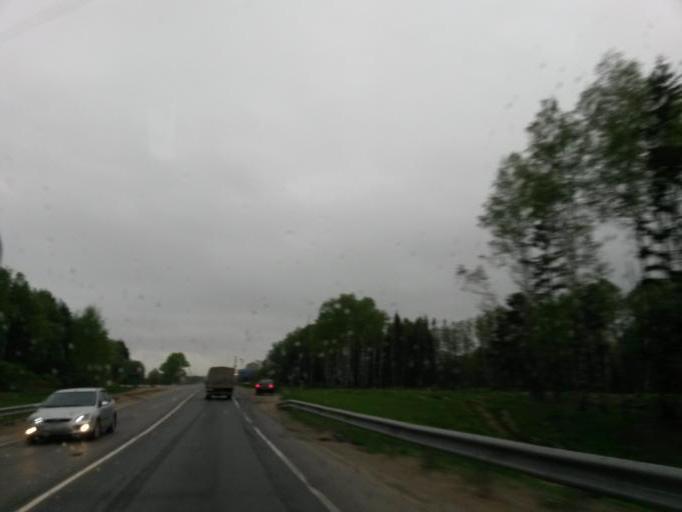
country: RU
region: Moskovskaya
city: L'vovskiy
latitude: 55.3315
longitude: 37.5805
